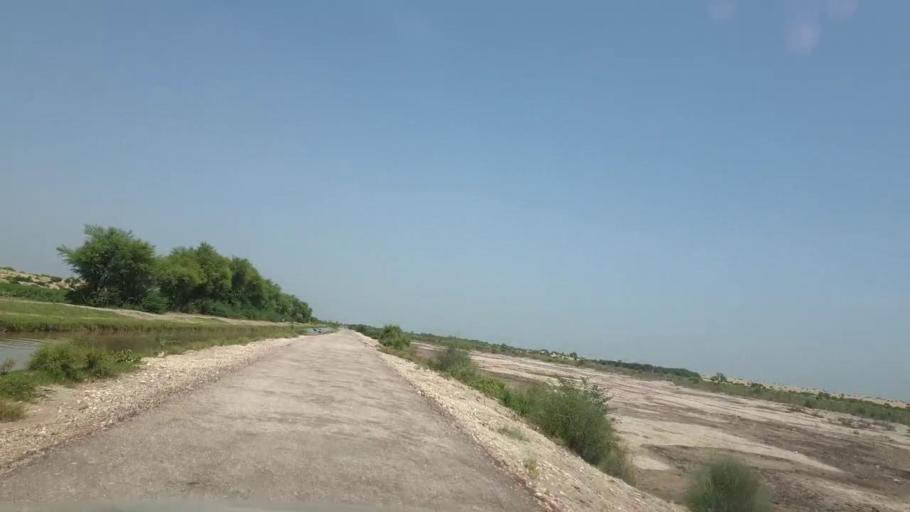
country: PK
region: Sindh
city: Rohri
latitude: 27.6176
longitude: 69.0989
